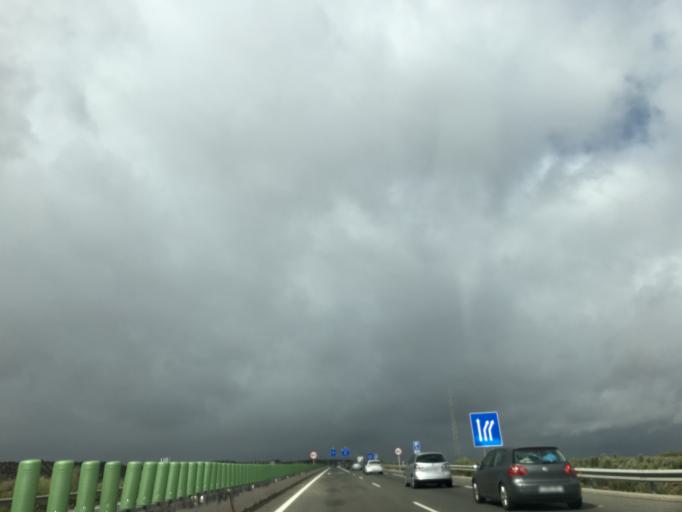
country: ES
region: Andalusia
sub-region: Provincia de Jaen
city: Bailen
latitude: 38.1157
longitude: -3.7546
